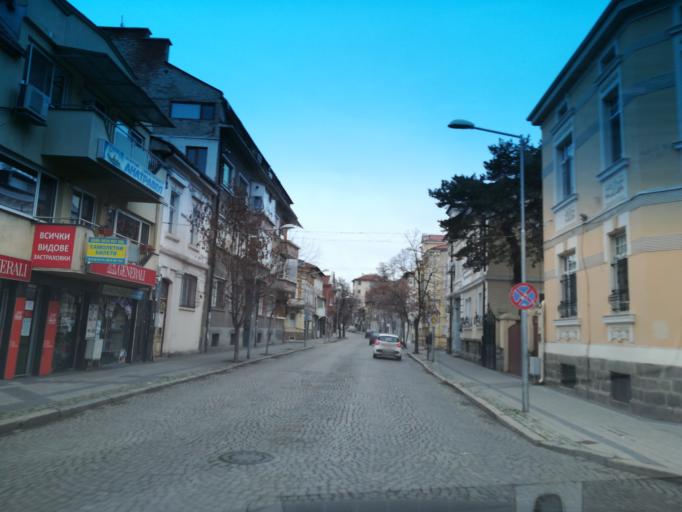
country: BG
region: Plovdiv
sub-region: Obshtina Plovdiv
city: Plovdiv
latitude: 42.1446
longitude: 24.7447
